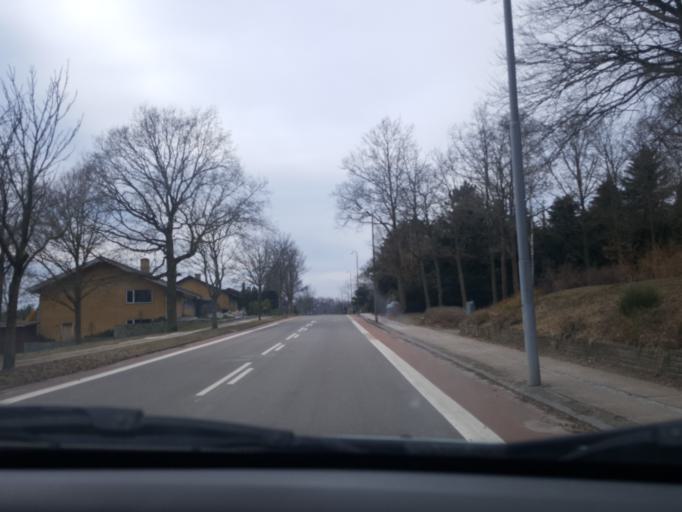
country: DK
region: Zealand
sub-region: Kalundborg Kommune
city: Kalundborg
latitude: 55.6877
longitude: 11.0820
